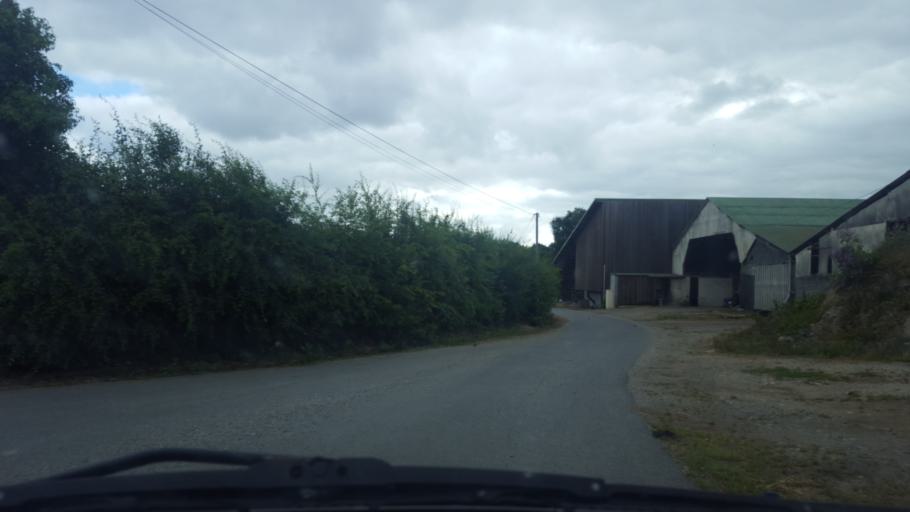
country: FR
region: Pays de la Loire
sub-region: Departement de la Loire-Atlantique
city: Saint-Philbert-de-Grand-Lieu
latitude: 47.0111
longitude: -1.6718
